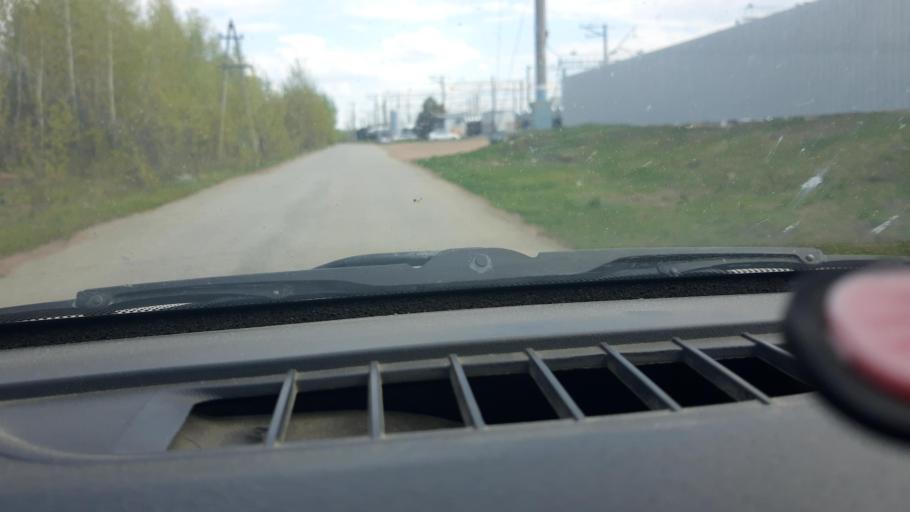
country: RU
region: Bashkortostan
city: Avdon
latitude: 54.6489
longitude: 55.8374
